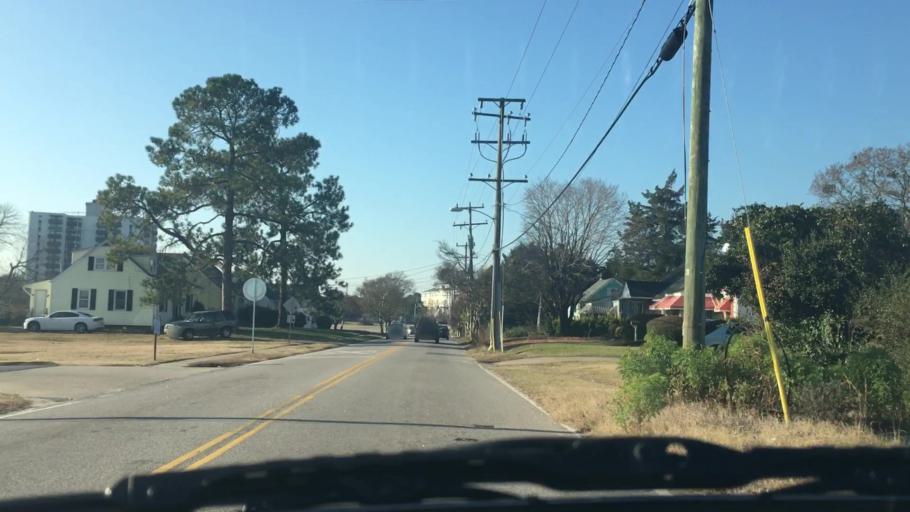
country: US
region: Virginia
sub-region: City of Norfolk
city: Norfolk
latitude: 36.8899
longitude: -76.2551
